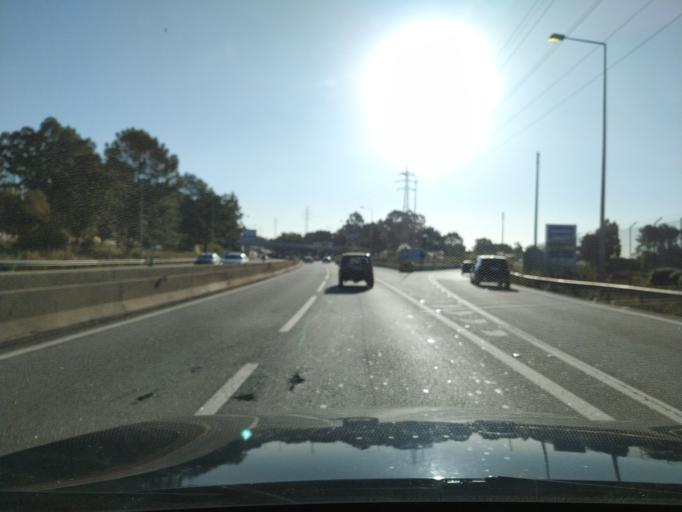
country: PT
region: Porto
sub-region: Vila Nova de Gaia
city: Vila Nova de Gaia
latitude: 41.1160
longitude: -8.6293
